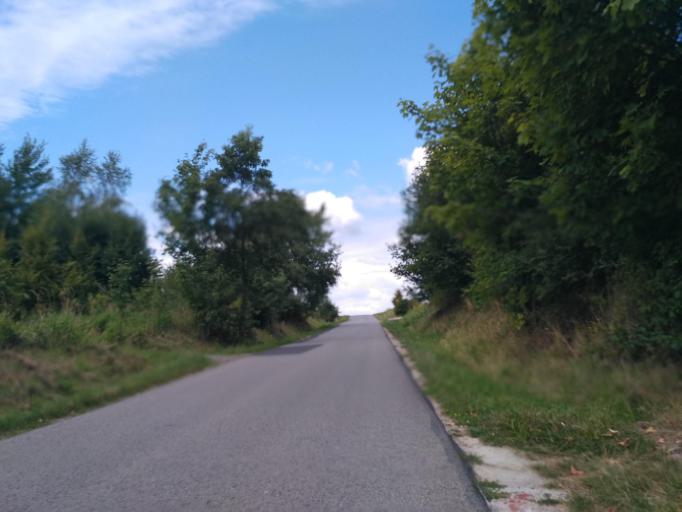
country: PL
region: Subcarpathian Voivodeship
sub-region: Powiat rzeszowski
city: Hyzne
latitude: 49.9135
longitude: 22.2166
